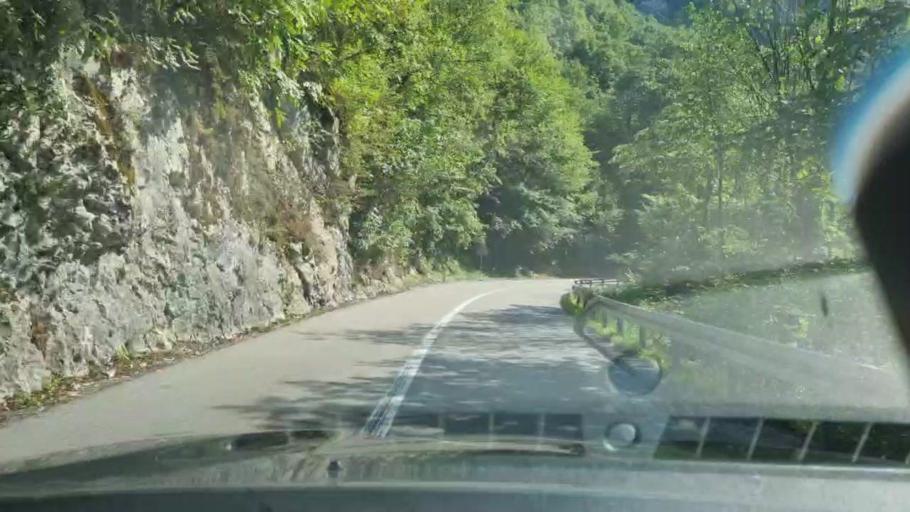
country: BA
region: Federation of Bosnia and Herzegovina
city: Bosanska Krupa
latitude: 44.8669
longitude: 16.0959
